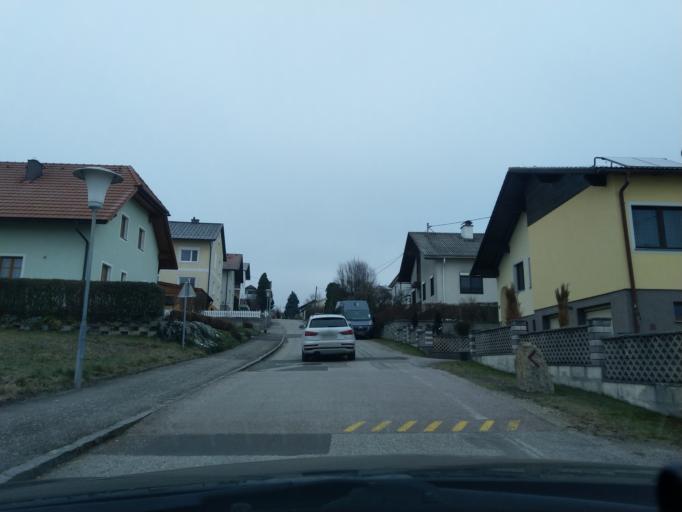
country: AT
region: Upper Austria
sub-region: Politischer Bezirk Urfahr-Umgebung
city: Engerwitzdorf
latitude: 48.3652
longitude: 14.5243
